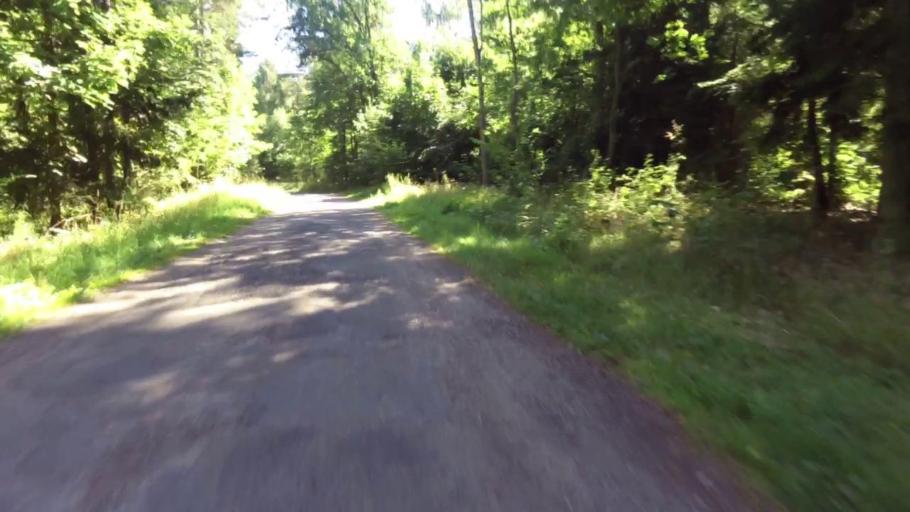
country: PL
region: West Pomeranian Voivodeship
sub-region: Powiat drawski
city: Czaplinek
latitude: 53.5181
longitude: 16.1873
